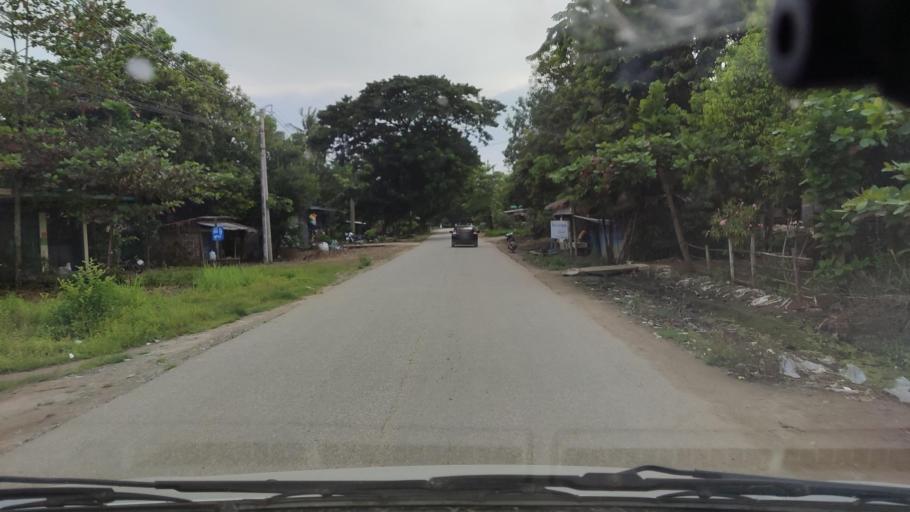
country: MM
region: Bago
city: Pyu
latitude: 18.5454
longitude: 96.5371
